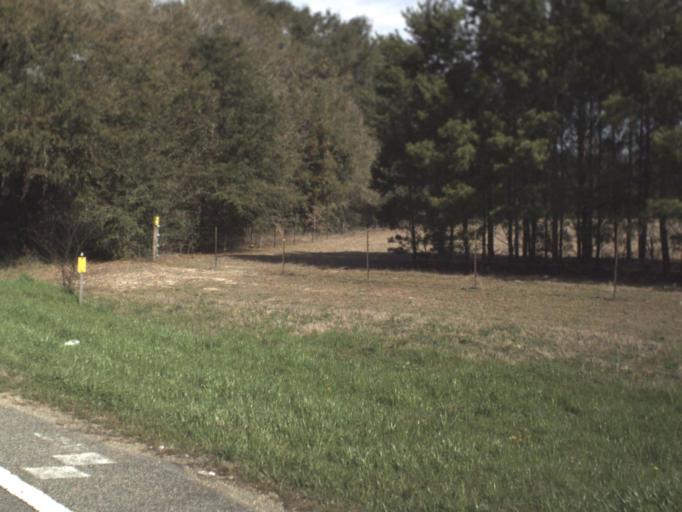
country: US
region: Florida
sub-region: Jackson County
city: Malone
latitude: 30.9880
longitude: -85.1888
